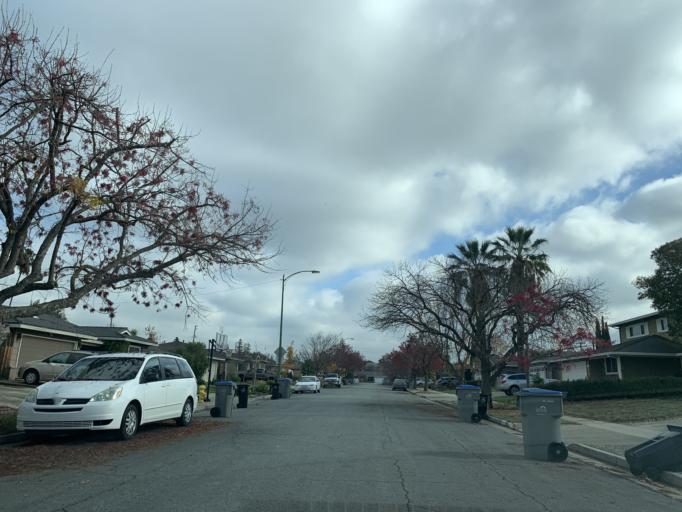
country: US
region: California
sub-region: Santa Clara County
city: Cambrian Park
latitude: 37.2443
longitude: -121.9163
